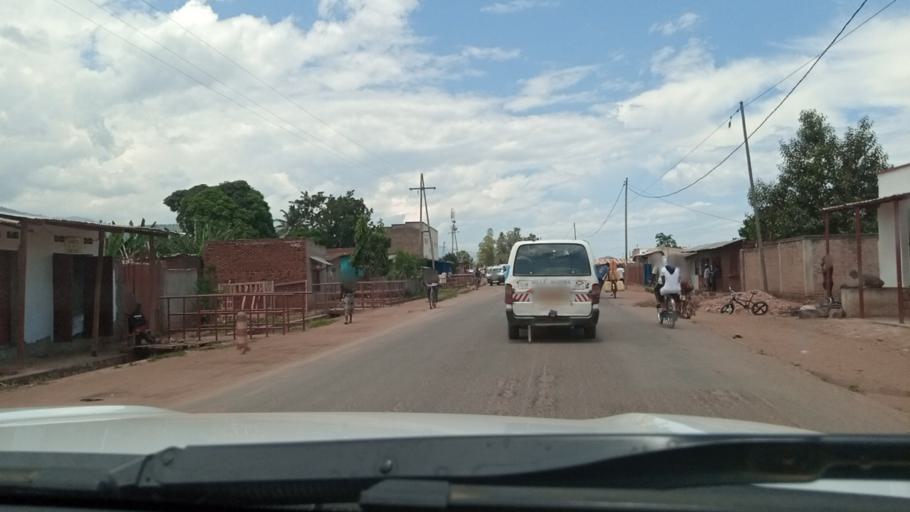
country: BI
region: Bujumbura Mairie
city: Bujumbura
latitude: -3.4681
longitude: 29.3497
